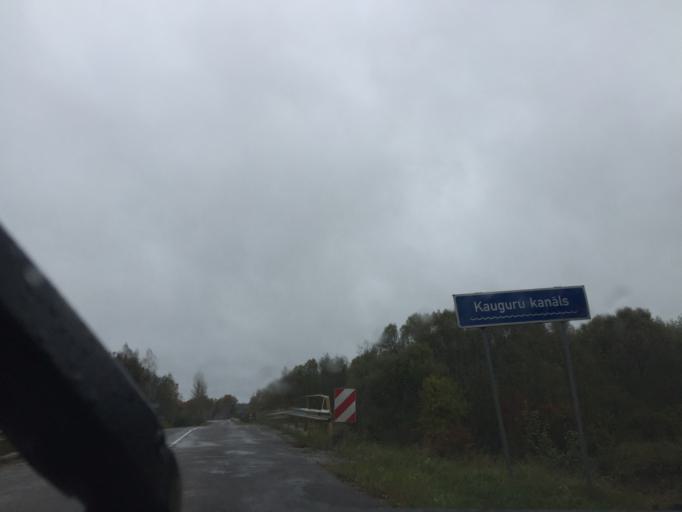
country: LV
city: Tireli
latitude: 56.8295
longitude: 23.5588
